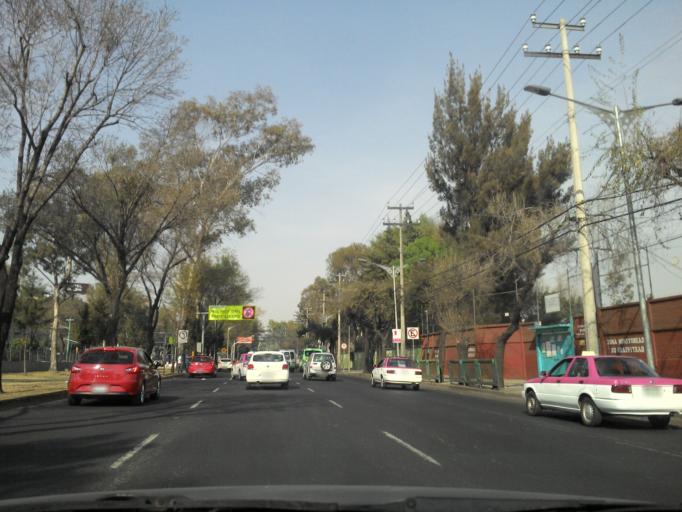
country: MX
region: Mexico City
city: Tlalpan
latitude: 19.3040
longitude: -99.1451
